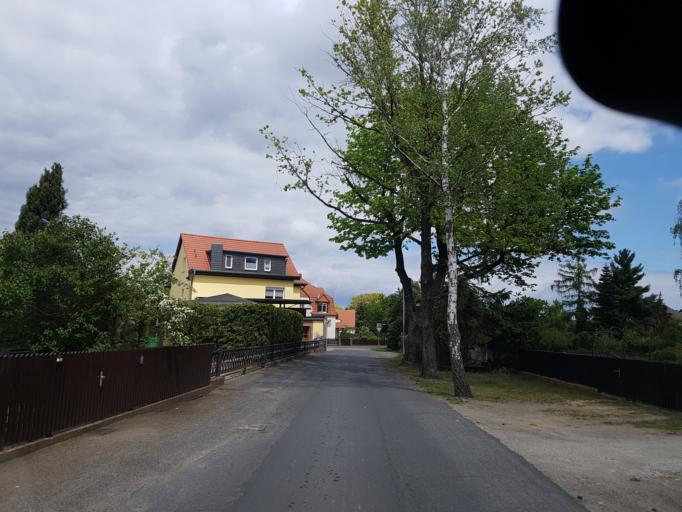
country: DE
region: Brandenburg
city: Altdobern
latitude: 51.6473
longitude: 14.0247
